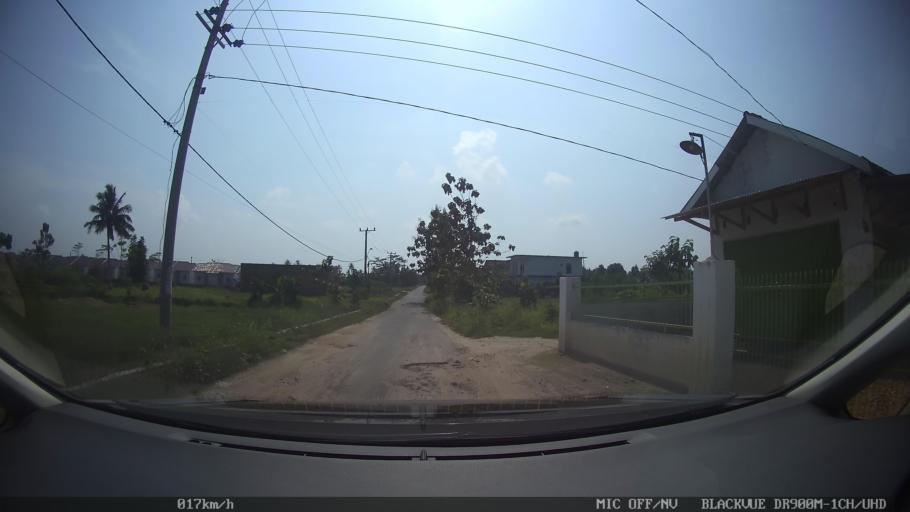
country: ID
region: Lampung
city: Natar
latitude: -5.2650
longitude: 105.2040
